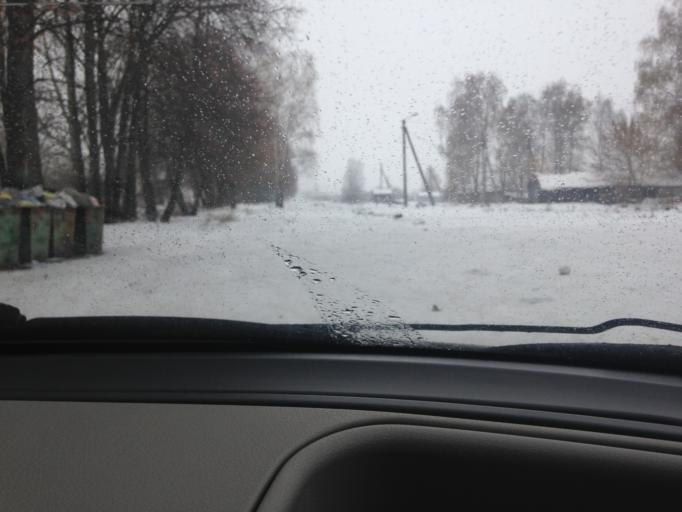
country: RU
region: Tula
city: Shchekino
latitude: 53.8515
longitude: 37.4778
